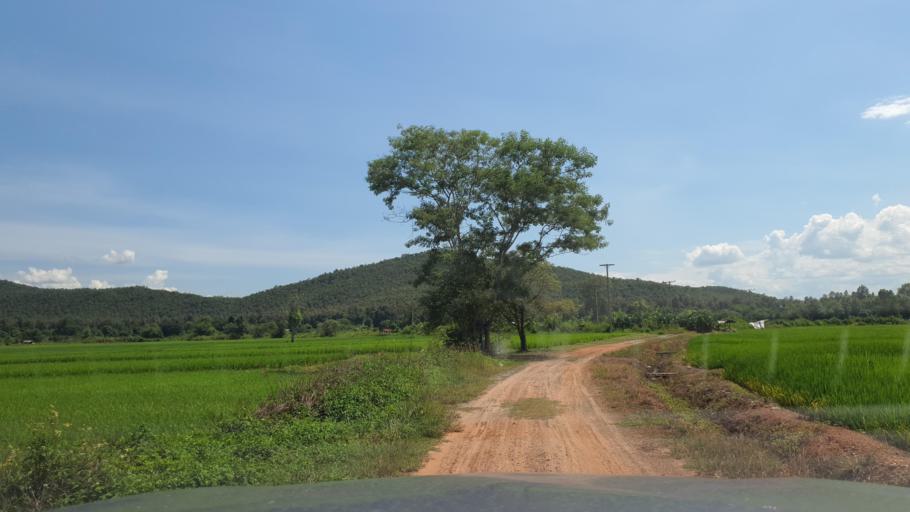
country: TH
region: Chiang Mai
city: Mae On
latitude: 18.7826
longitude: 99.1876
